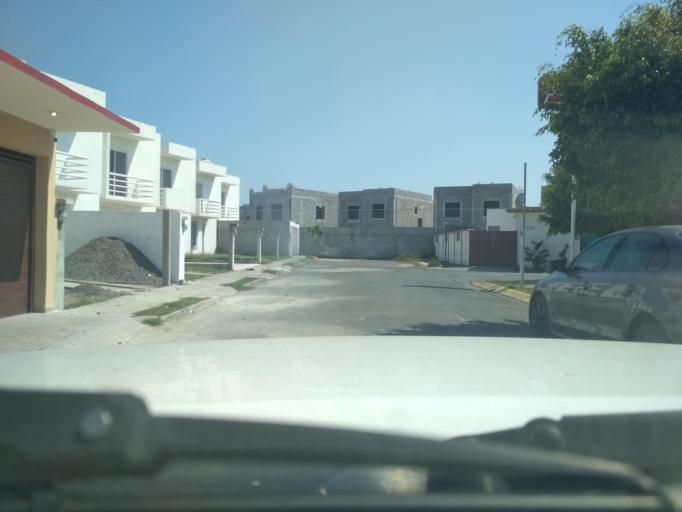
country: MX
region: Veracruz
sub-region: Veracruz
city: Lomas de Rio Medio Cuatro
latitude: 19.1814
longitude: -96.1916
